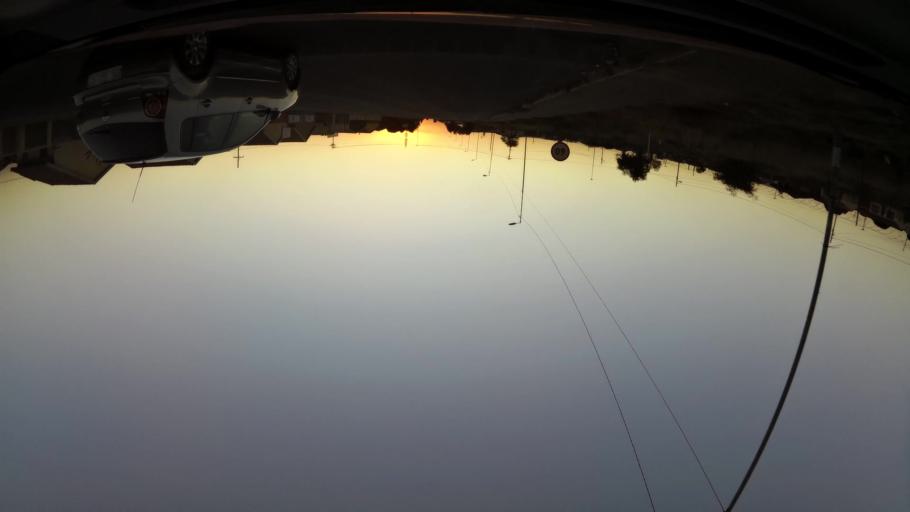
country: ZA
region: North-West
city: Ga-Rankuwa
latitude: -25.6063
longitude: 28.0023
